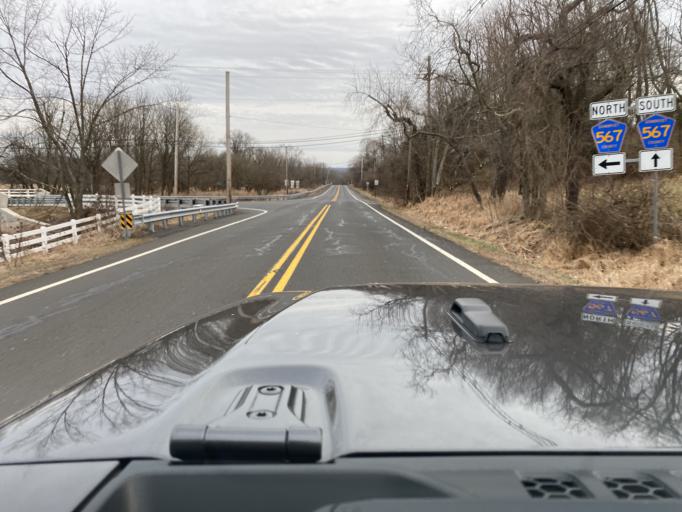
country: US
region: New Jersey
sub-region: Somerset County
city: Bloomingdale
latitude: 40.5203
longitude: -74.7363
